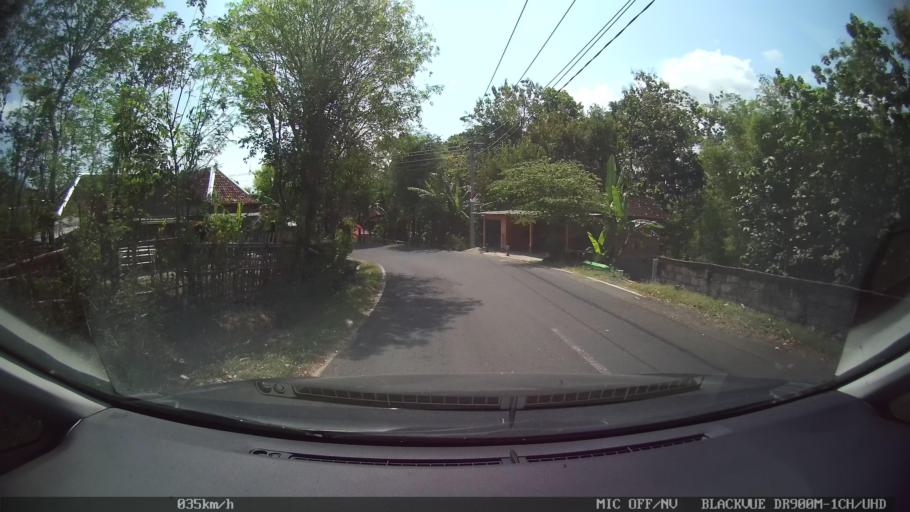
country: ID
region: Daerah Istimewa Yogyakarta
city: Pundong
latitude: -7.9573
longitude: 110.3740
